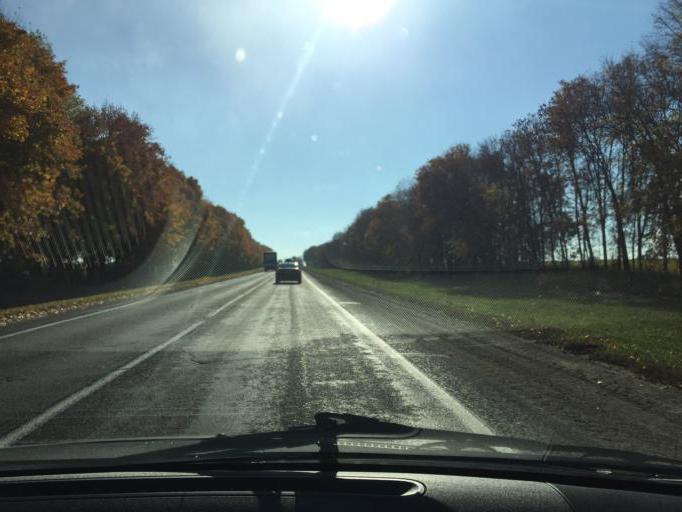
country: BY
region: Minsk
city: Salihorsk
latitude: 52.8838
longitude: 27.4695
